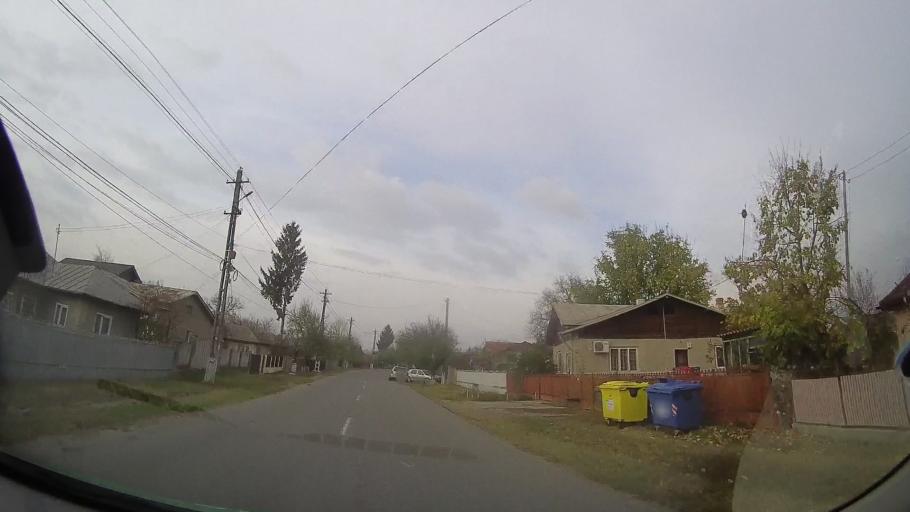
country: RO
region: Prahova
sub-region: Comuna Gorgota
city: Potigrafu
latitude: 44.7771
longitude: 26.1044
